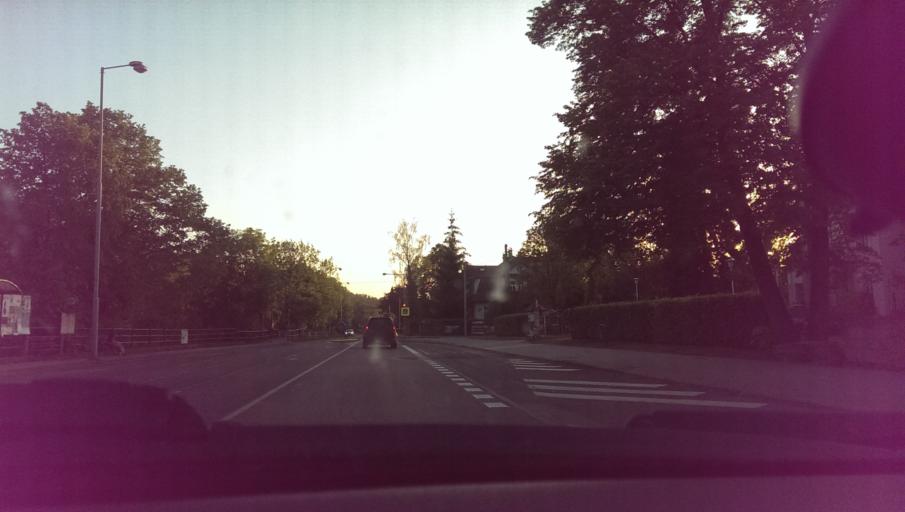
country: CZ
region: Zlin
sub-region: Okres Vsetin
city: Roznov pod Radhostem
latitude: 49.4626
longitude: 18.1438
